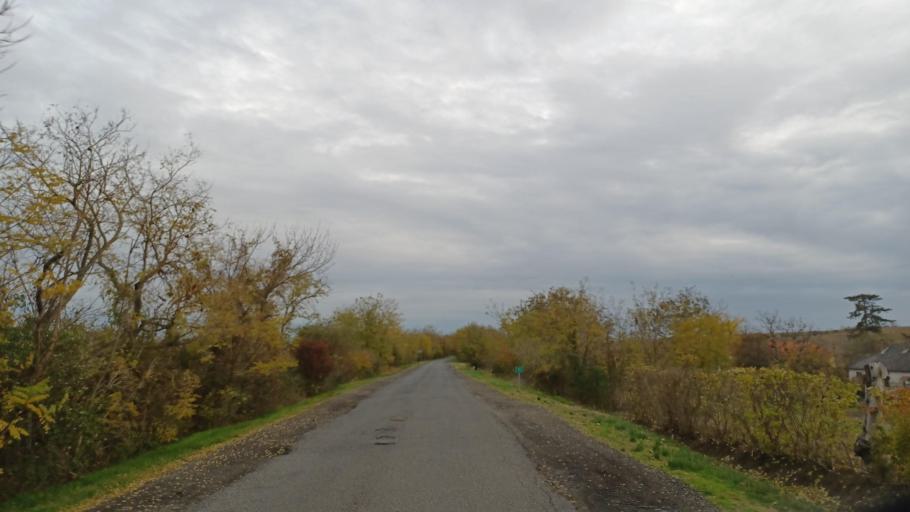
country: HU
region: Tolna
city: Nagydorog
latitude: 46.6847
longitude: 18.5975
